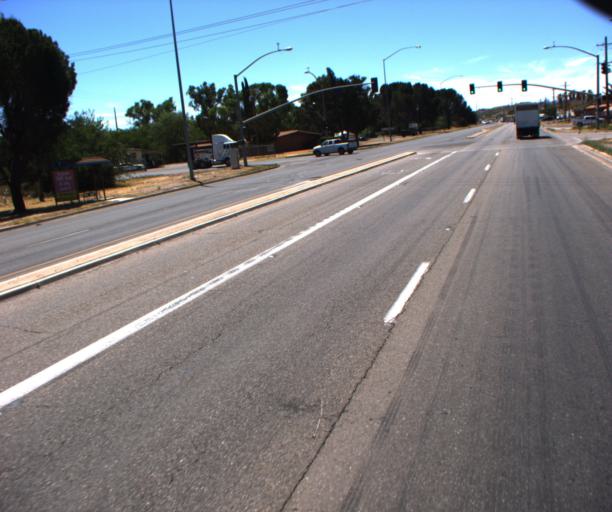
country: US
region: Arizona
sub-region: Santa Cruz County
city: Nogales
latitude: 31.3875
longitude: -110.9507
